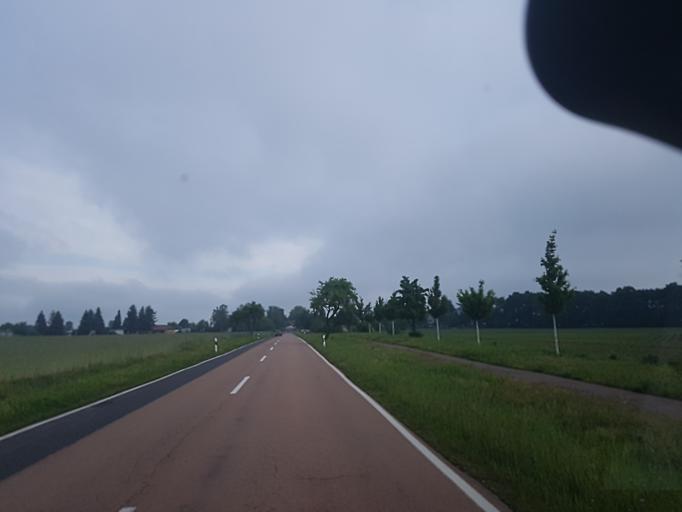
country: DE
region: Saxony-Anhalt
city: Klieken
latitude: 51.9779
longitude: 12.3485
